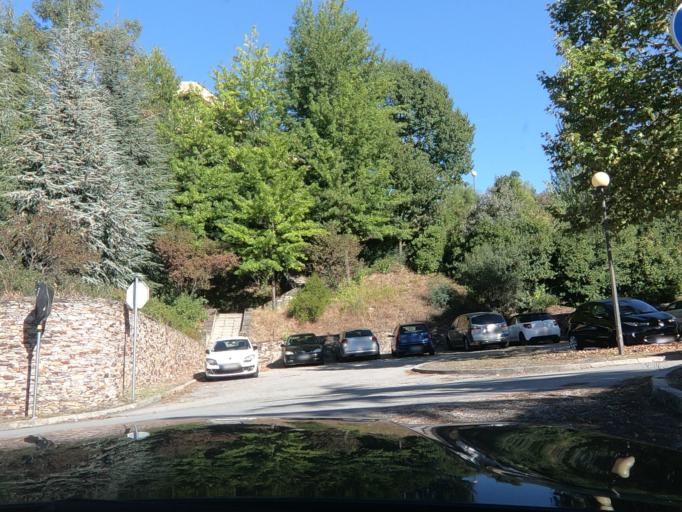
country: PT
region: Vila Real
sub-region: Vila Real
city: Vila Real
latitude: 41.2850
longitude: -7.7453
